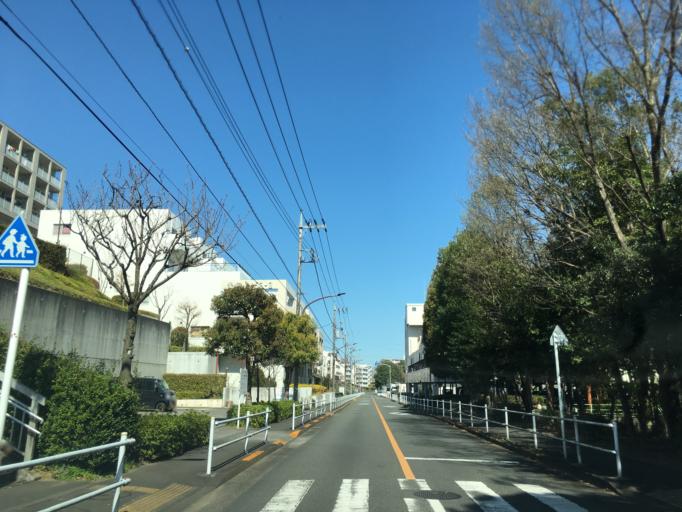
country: JP
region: Tokyo
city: Hino
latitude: 35.6312
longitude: 139.4300
